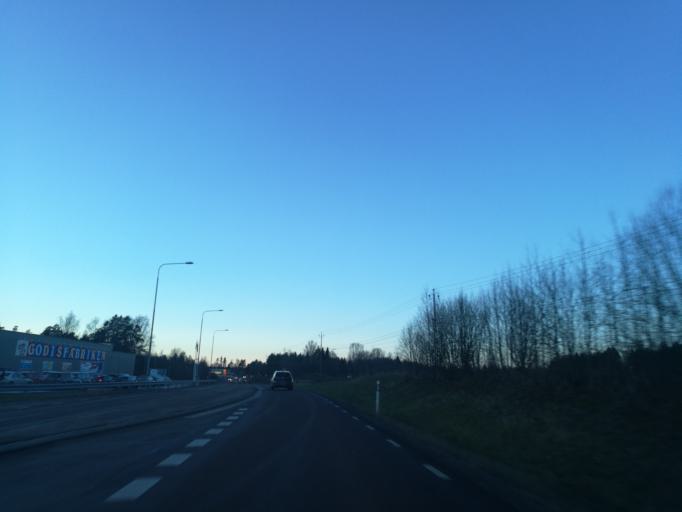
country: SE
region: Vaermland
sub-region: Eda Kommun
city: Charlottenberg
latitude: 59.9211
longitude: 12.2687
